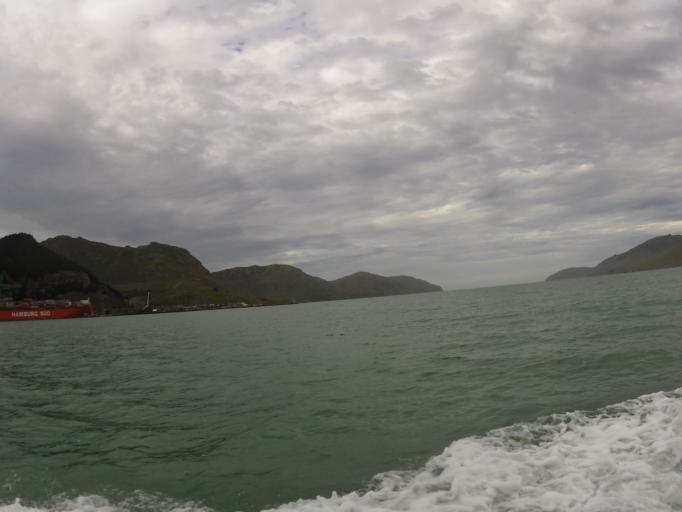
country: NZ
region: Canterbury
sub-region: Christchurch City
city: Christchurch
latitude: -43.6156
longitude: 172.7248
